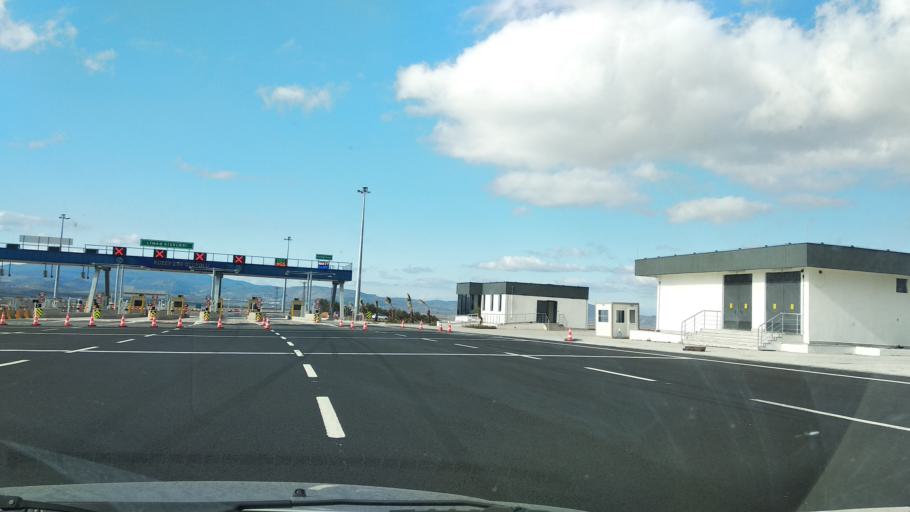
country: TR
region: Izmir
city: Zeytindag
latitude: 38.9733
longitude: 27.0547
